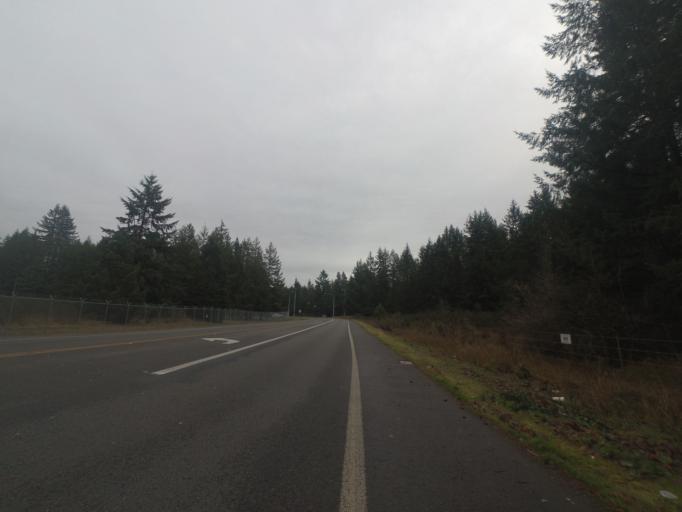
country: US
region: Washington
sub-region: Pierce County
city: McChord Air Force Base
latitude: 47.1151
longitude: -122.4960
